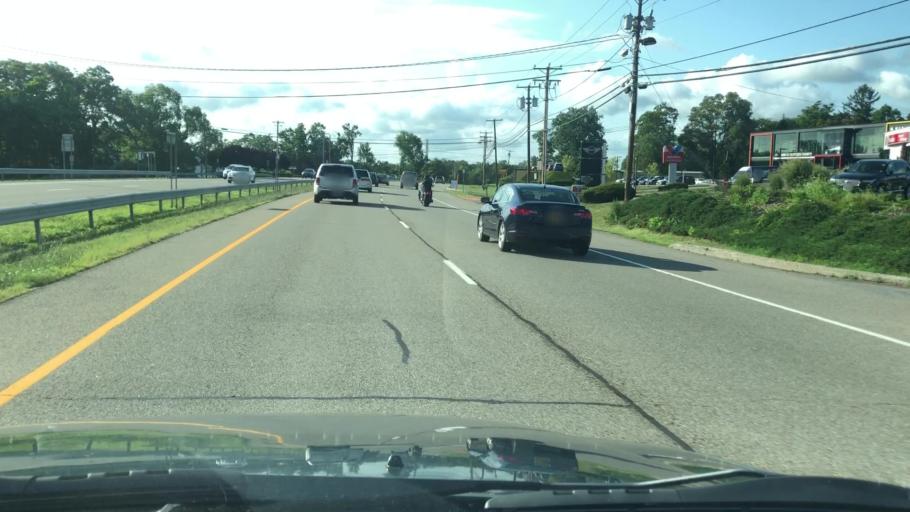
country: US
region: New York
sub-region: Dutchess County
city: Wappingers Falls
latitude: 41.5665
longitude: -73.9070
